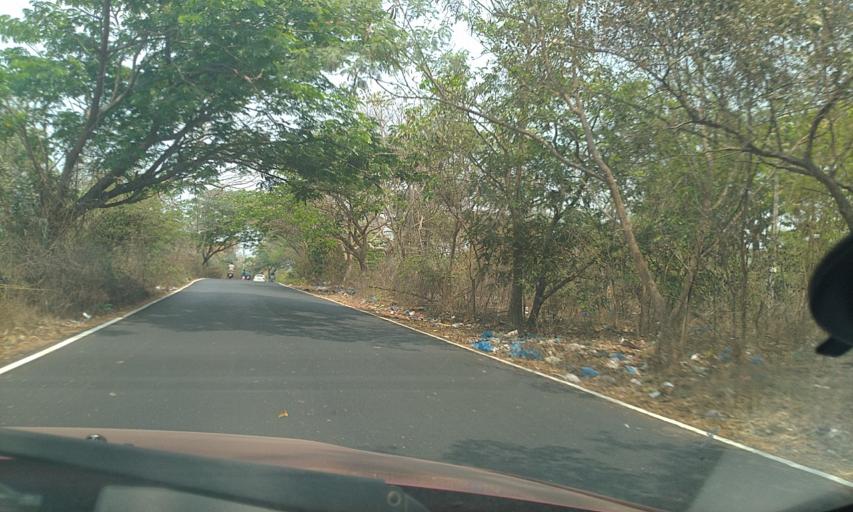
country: IN
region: Goa
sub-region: North Goa
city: Mapuca
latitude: 15.6094
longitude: 73.7973
